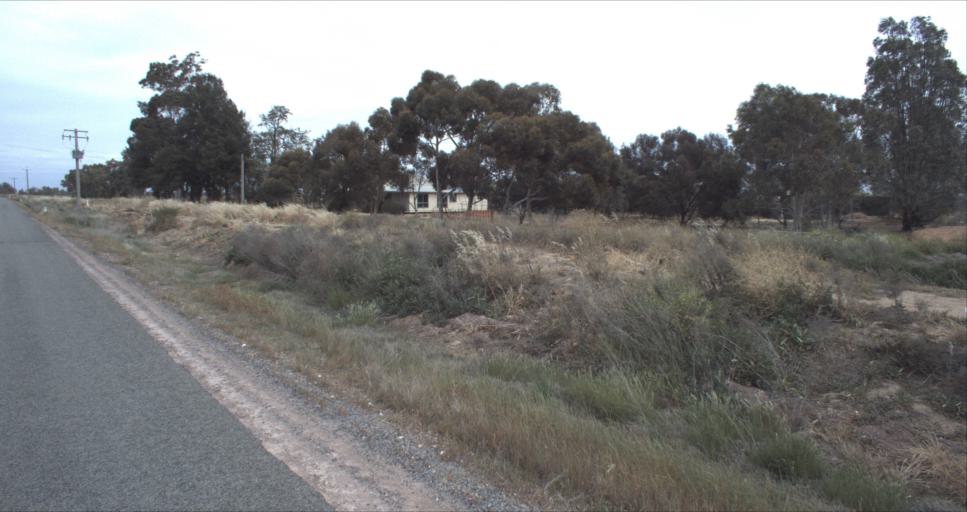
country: AU
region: New South Wales
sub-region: Leeton
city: Leeton
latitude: -34.4314
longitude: 146.3773
